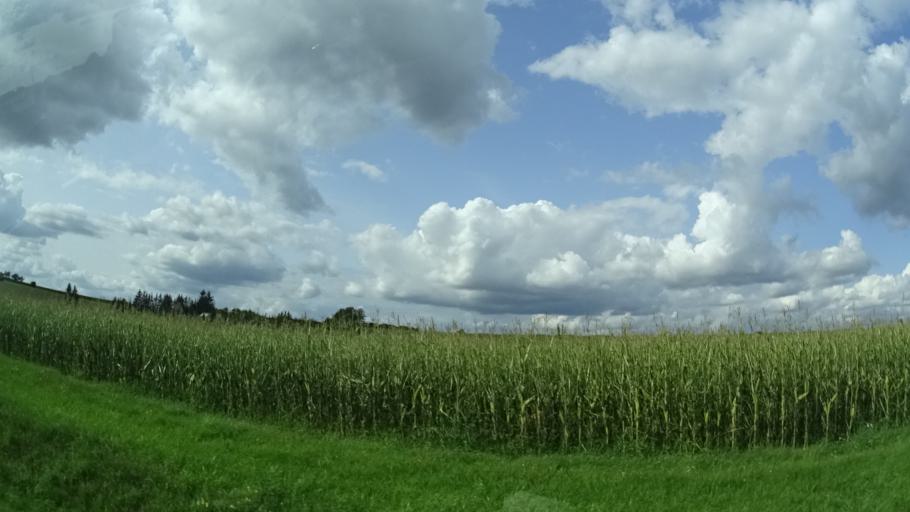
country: DE
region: Bavaria
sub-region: Regierungsbezirk Unterfranken
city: Werneck
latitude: 49.9855
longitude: 10.1066
